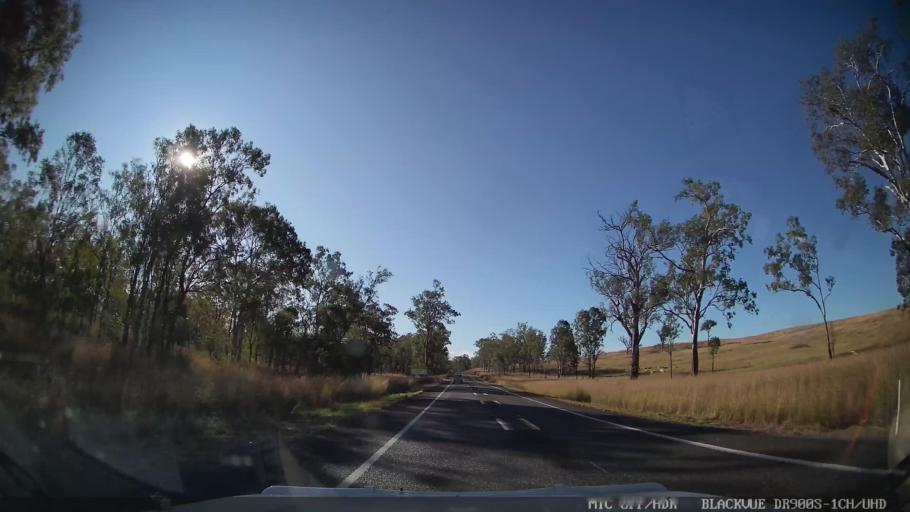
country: AU
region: Queensland
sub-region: Bundaberg
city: Sharon
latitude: -24.8339
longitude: 151.7095
